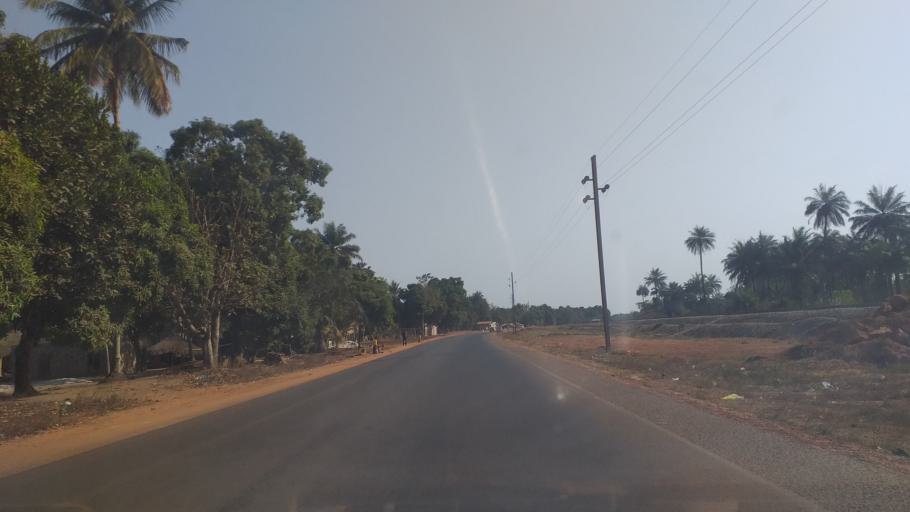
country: GN
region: Boke
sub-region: Boke Prefecture
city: Kamsar
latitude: 10.7357
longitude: -14.5159
